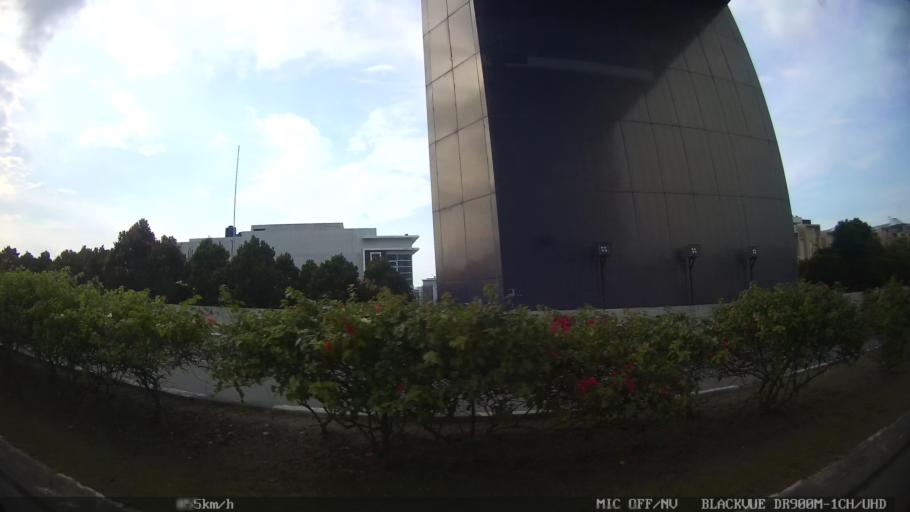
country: ID
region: North Sumatra
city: Medan
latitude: 3.6059
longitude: 98.7239
